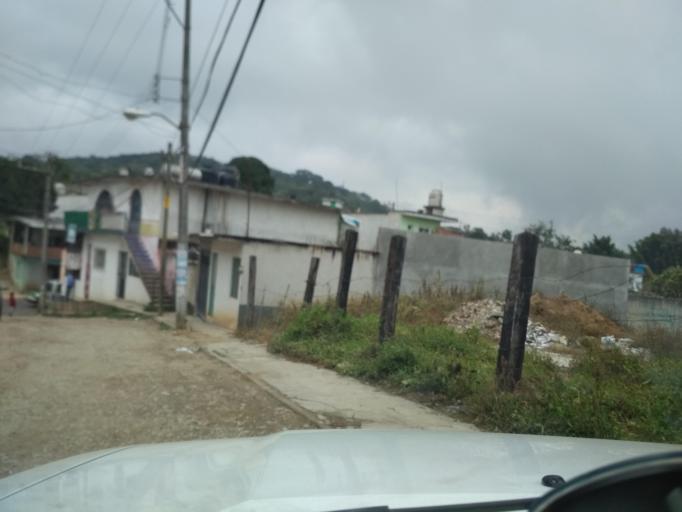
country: MX
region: Veracruz
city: El Castillo
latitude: 19.5470
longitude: -96.8638
